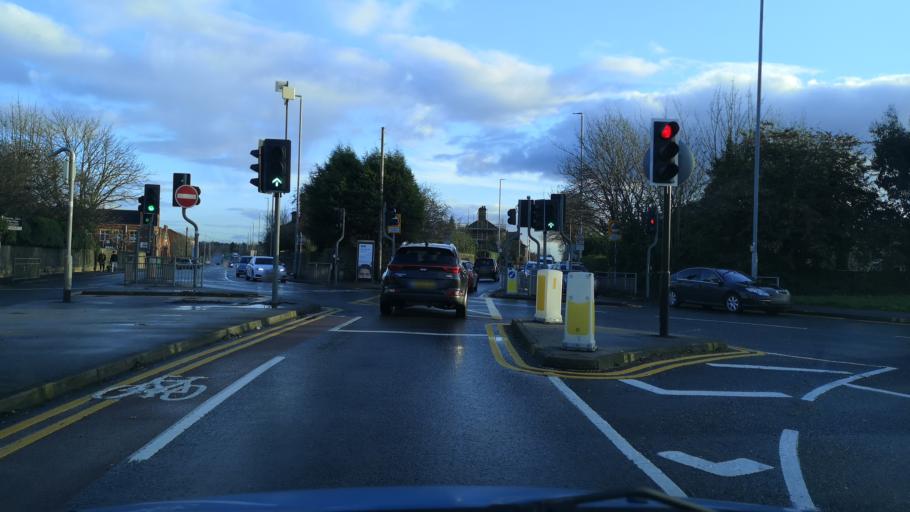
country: GB
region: England
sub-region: City and Borough of Leeds
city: Morley
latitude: 53.7355
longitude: -1.5942
